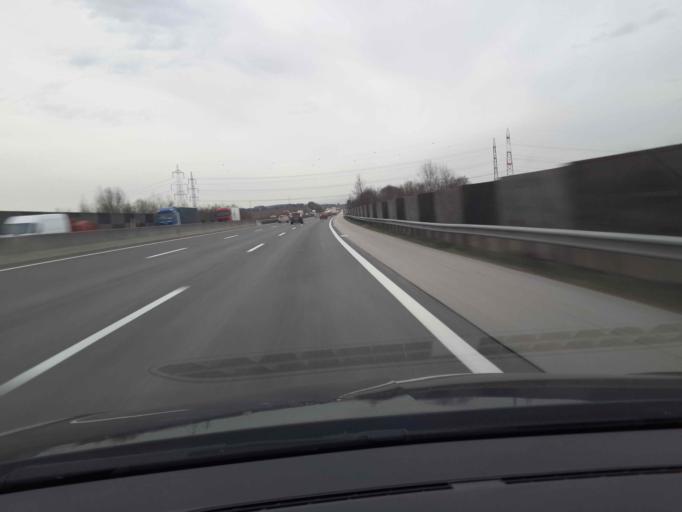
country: AT
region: Lower Austria
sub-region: Politischer Bezirk Amstetten
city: Strengberg
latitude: 48.1181
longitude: 14.6221
